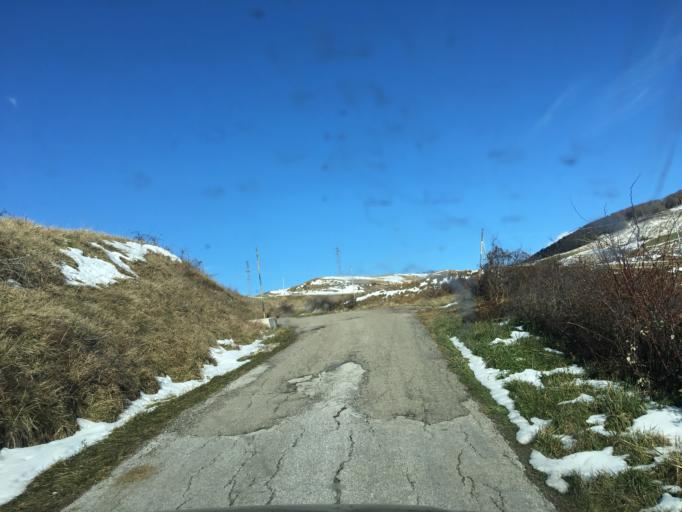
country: IT
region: Molise
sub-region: Provincia di Isernia
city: Agnone
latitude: 41.8532
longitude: 14.3565
